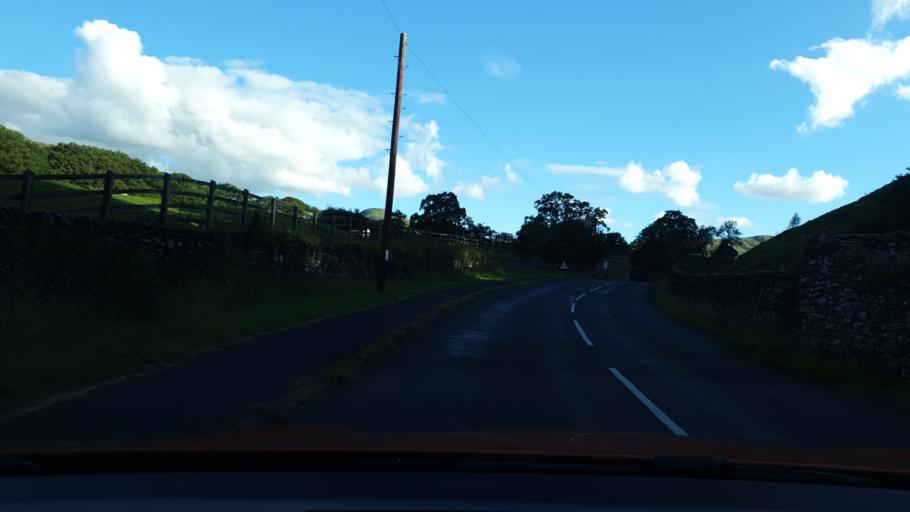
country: GB
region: England
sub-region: Cumbria
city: Ambleside
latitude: 54.5310
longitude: -2.9311
